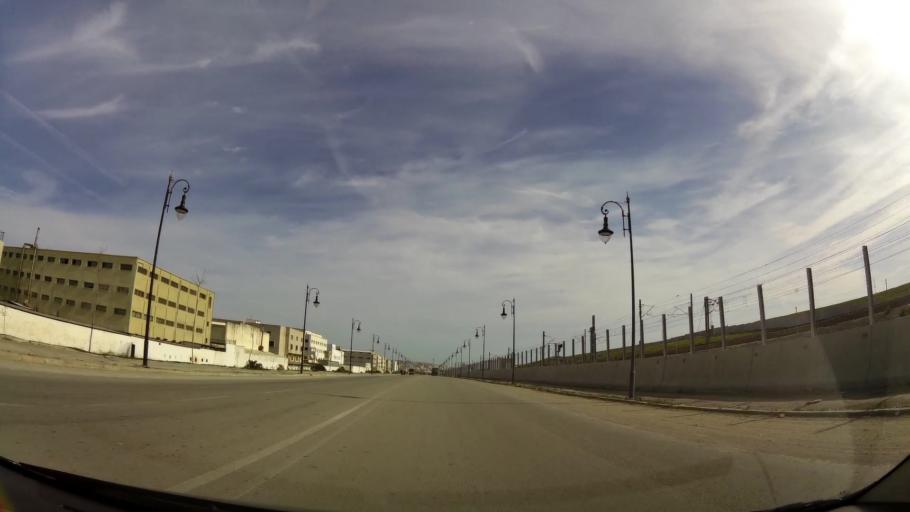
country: MA
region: Tanger-Tetouan
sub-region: Tanger-Assilah
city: Tangier
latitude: 35.7366
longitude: -5.7955
